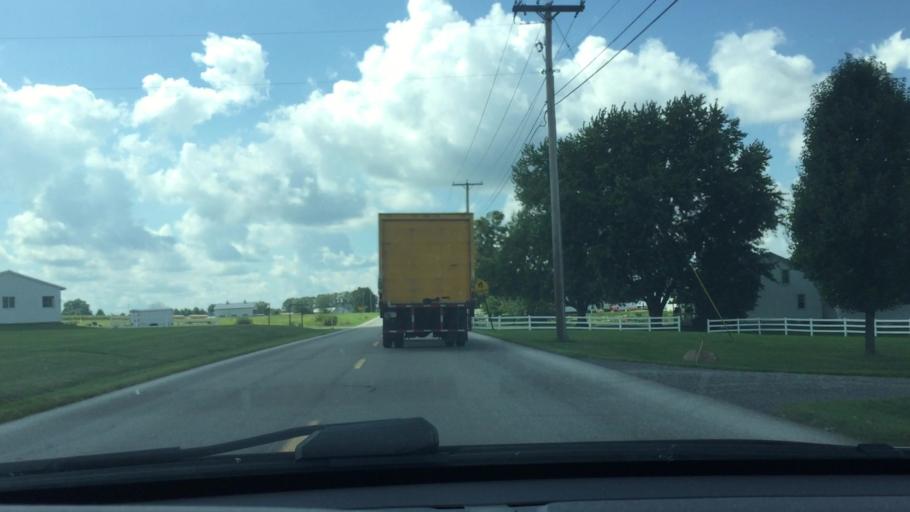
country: US
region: Pennsylvania
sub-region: Lawrence County
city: New Wilmington
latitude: 41.1205
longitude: -80.3652
